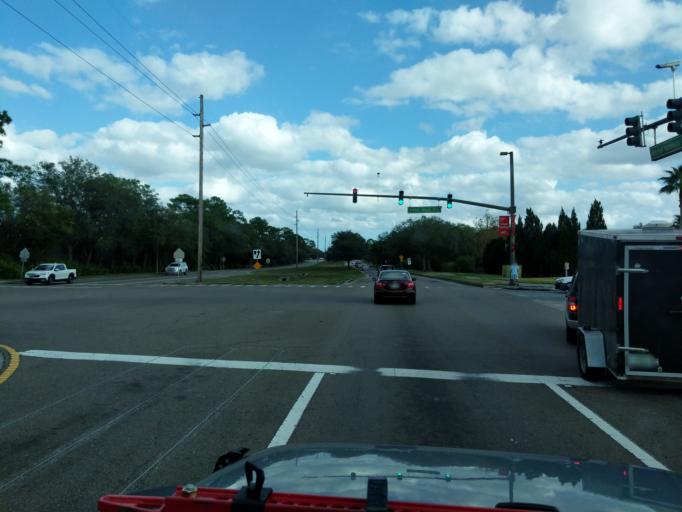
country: US
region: Florida
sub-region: Seminole County
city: Oviedo
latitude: 28.6559
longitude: -81.1891
